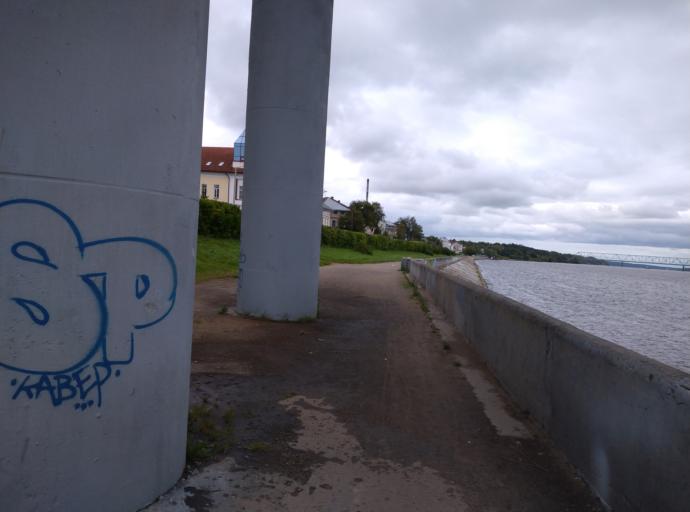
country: RU
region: Kostroma
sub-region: Kostromskoy Rayon
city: Kostroma
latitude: 57.7556
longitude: 40.9431
